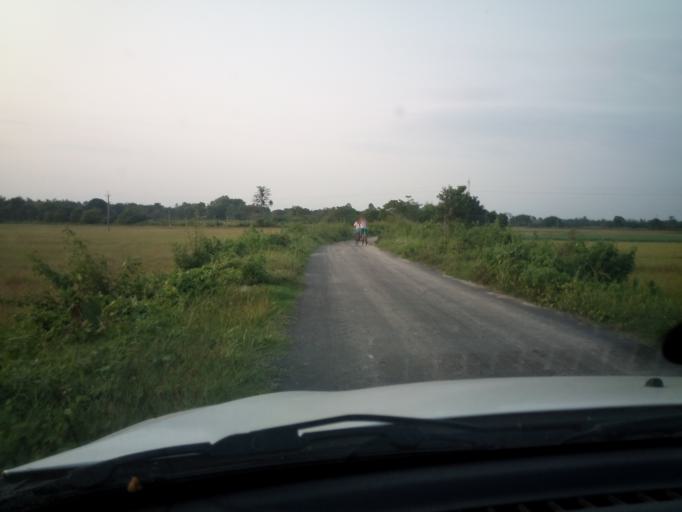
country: IN
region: Assam
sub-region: Udalguri
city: Udalguri
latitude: 26.6774
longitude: 92.1097
